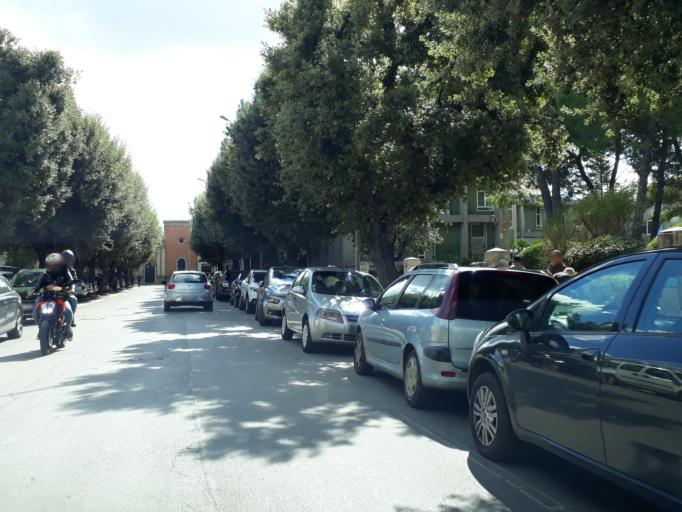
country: IT
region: Apulia
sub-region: Provincia di Bari
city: Rutigliano
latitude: 41.0115
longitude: 17.0081
